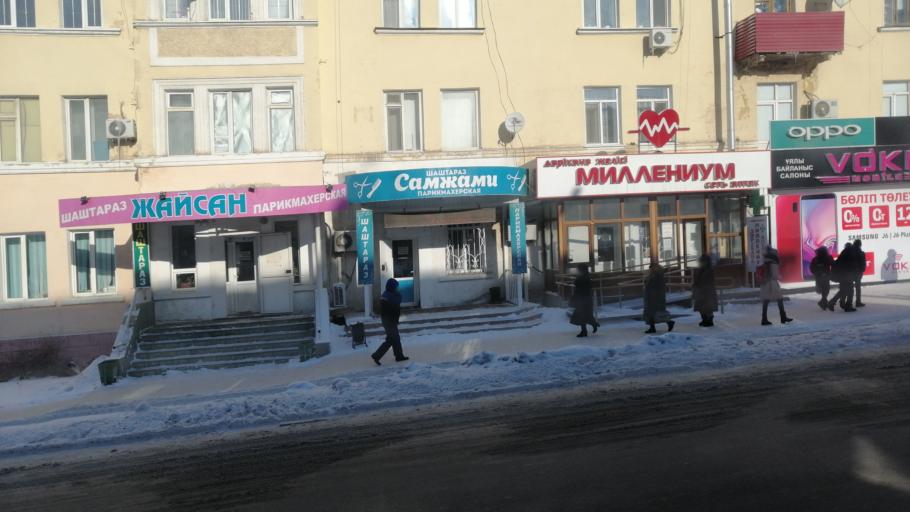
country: KZ
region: Aqtoebe
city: Aqtobe
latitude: 50.2810
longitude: 57.2265
